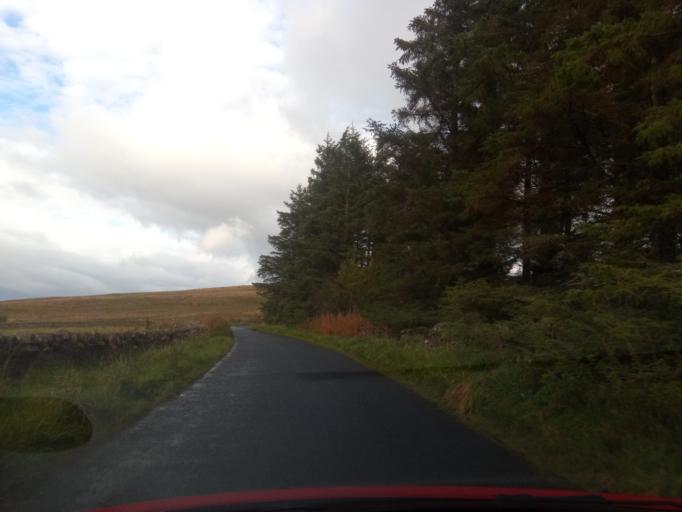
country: GB
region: Scotland
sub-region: The Scottish Borders
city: Galashiels
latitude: 55.6893
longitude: -2.8565
